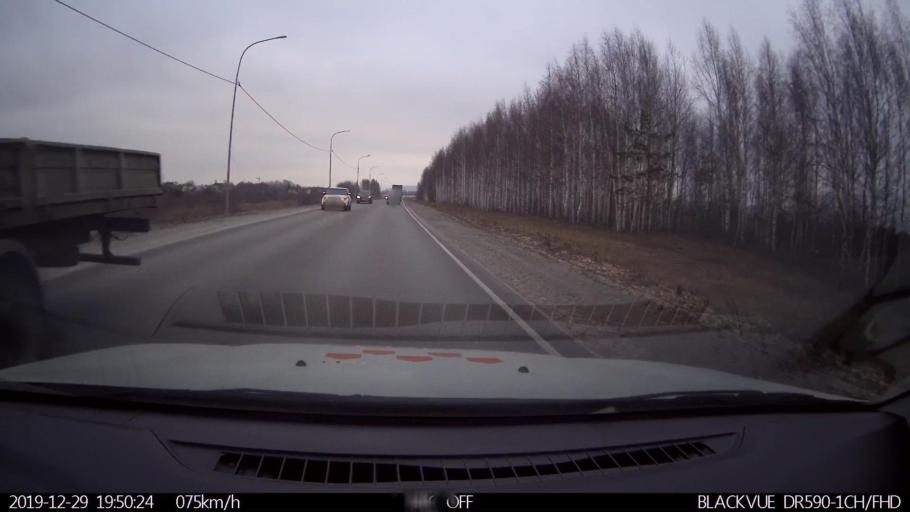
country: RU
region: Nizjnij Novgorod
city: Bor
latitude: 56.3685
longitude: 44.0283
